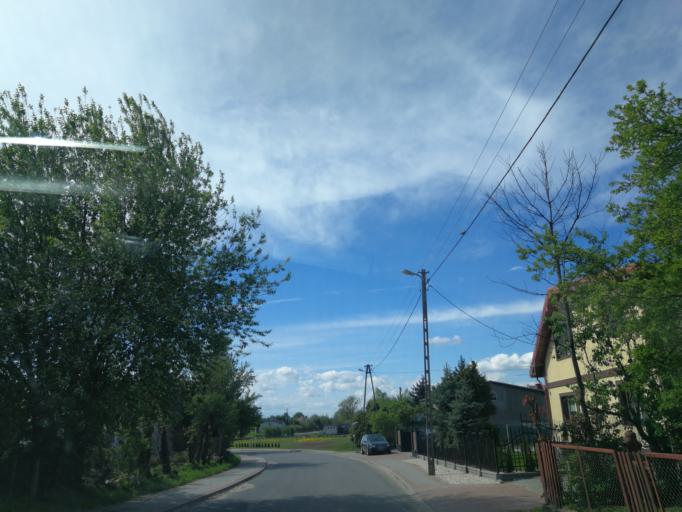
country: PL
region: Warmian-Masurian Voivodeship
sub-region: Powiat ilawski
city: Lubawa
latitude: 53.5987
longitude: 19.6988
